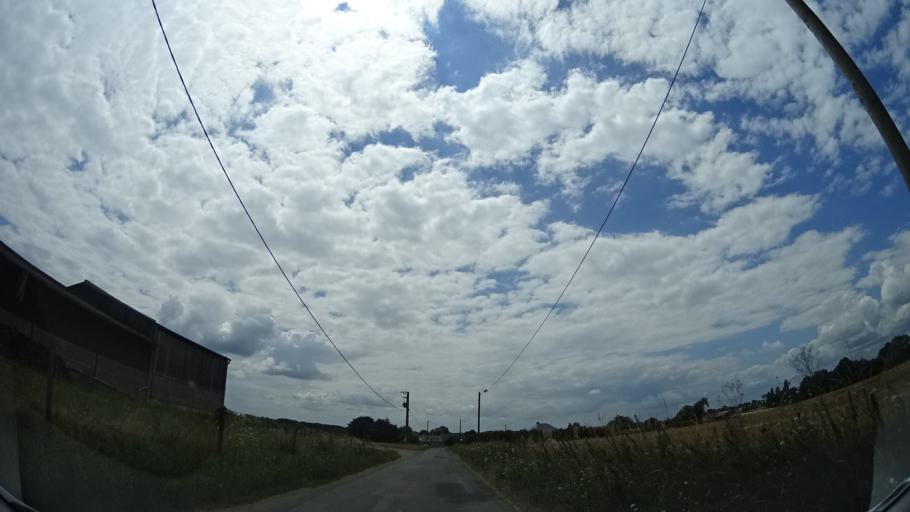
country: FR
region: Brittany
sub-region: Departement d'Ille-et-Vilaine
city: La Chapelle-des-Fougeretz
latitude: 48.1718
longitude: -1.7537
